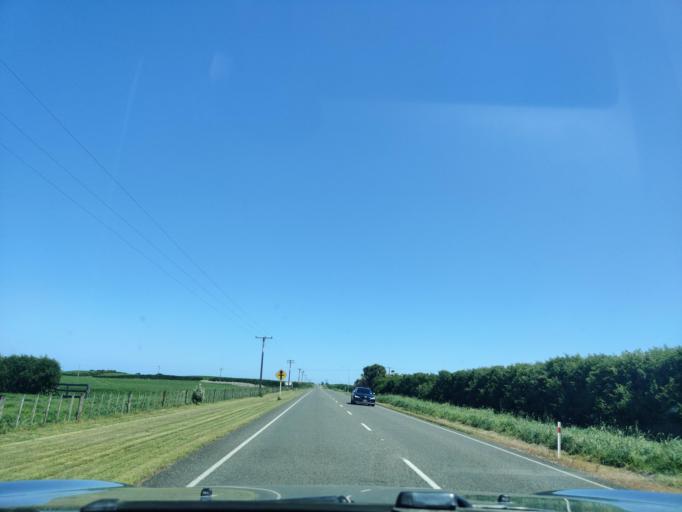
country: NZ
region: Taranaki
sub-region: South Taranaki District
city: Patea
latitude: -39.7467
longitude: 174.5106
